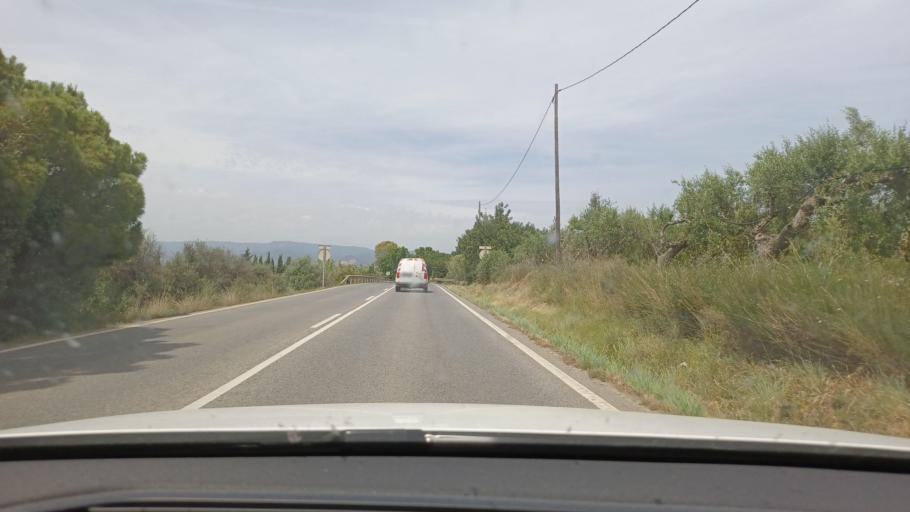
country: ES
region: Catalonia
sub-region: Provincia de Tarragona
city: Cambrils
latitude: 41.0968
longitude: 1.0828
